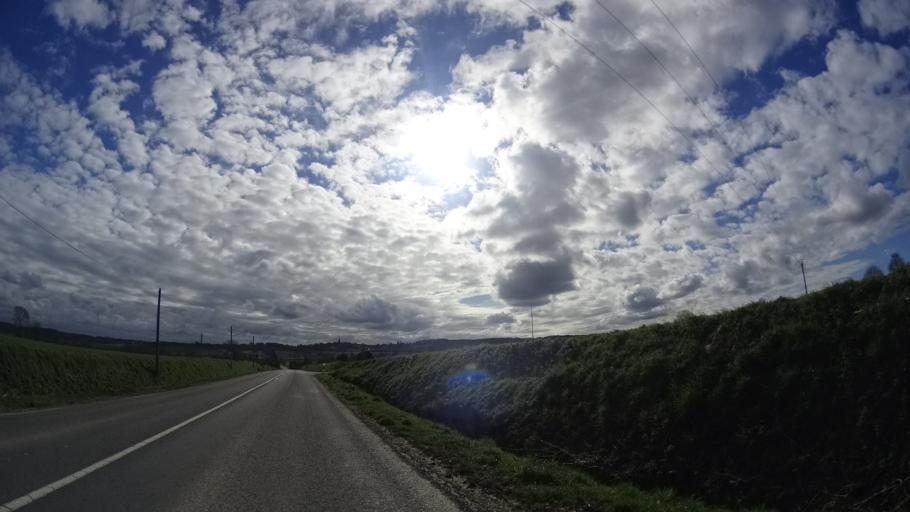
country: FR
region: Brittany
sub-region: Departement des Cotes-d'Armor
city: Plouasne
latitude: 48.3164
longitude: -1.9544
